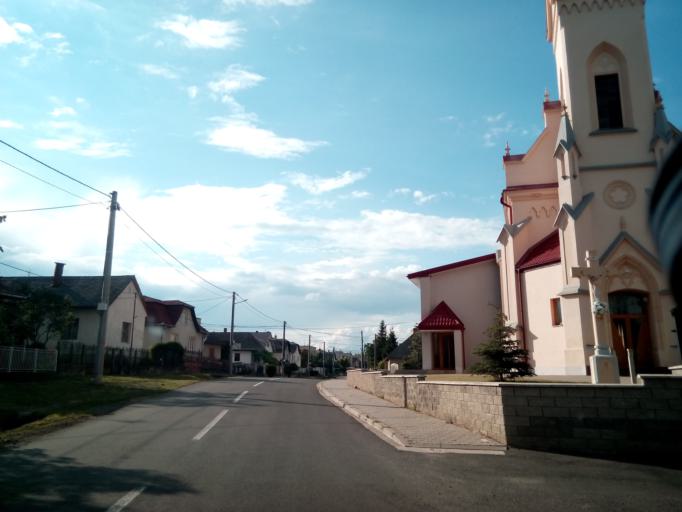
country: SK
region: Kosicky
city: Secovce
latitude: 48.5819
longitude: 21.5695
